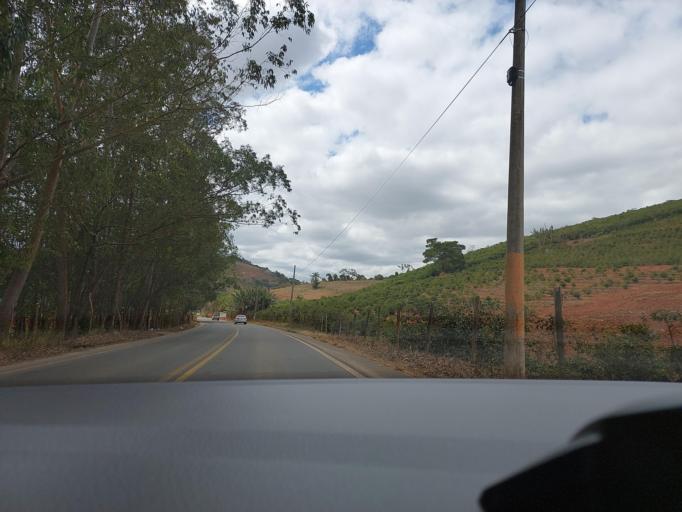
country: BR
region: Minas Gerais
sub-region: Vicosa
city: Vicosa
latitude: -20.8447
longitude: -42.6820
